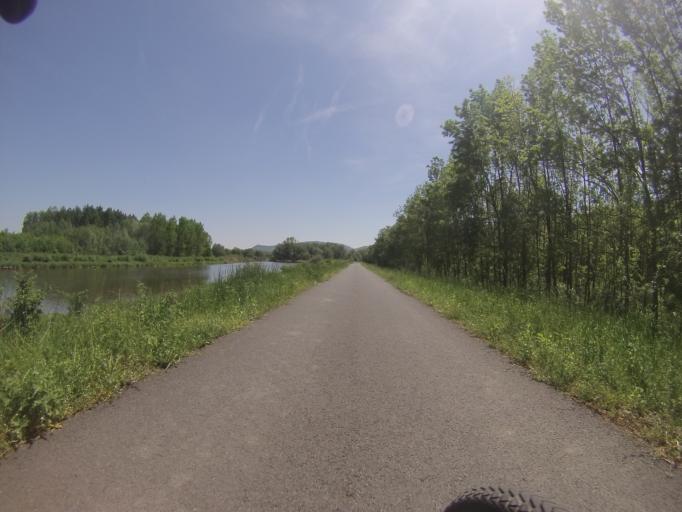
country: CZ
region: South Moravian
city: Vranovice
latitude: 48.9152
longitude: 16.6009
